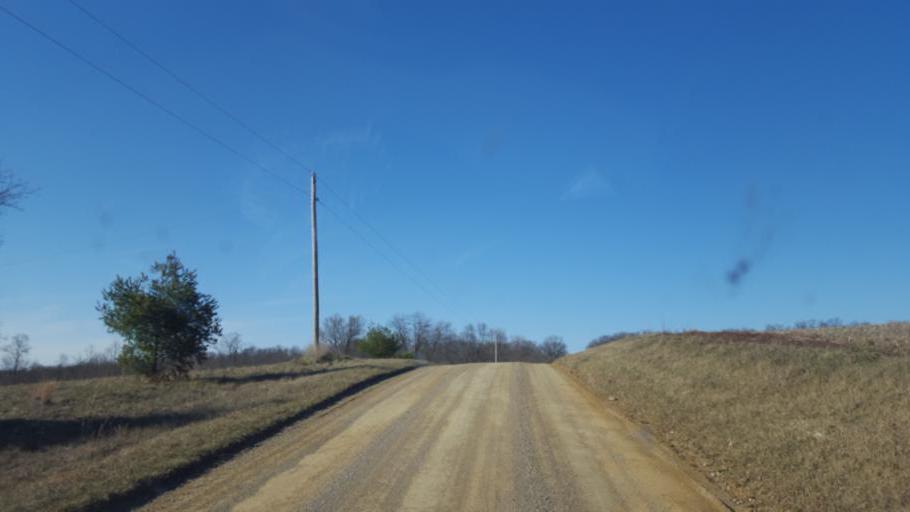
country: US
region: Ohio
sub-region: Knox County
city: Gambier
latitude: 40.4451
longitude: -82.3904
